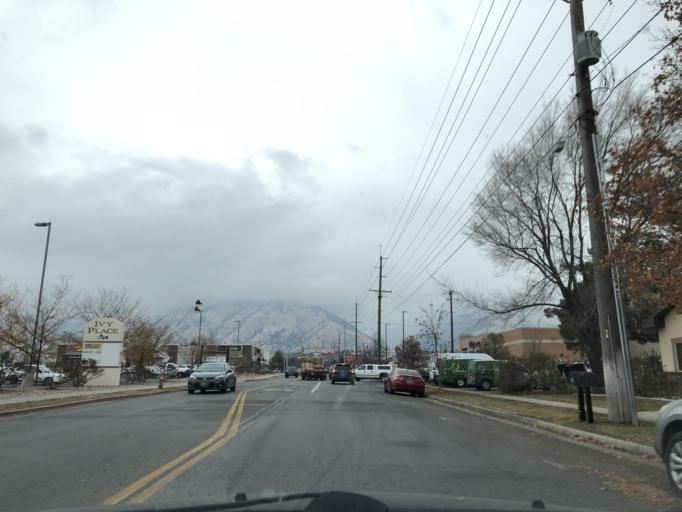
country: US
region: Utah
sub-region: Cache County
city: Logan
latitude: 41.7502
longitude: -111.8366
